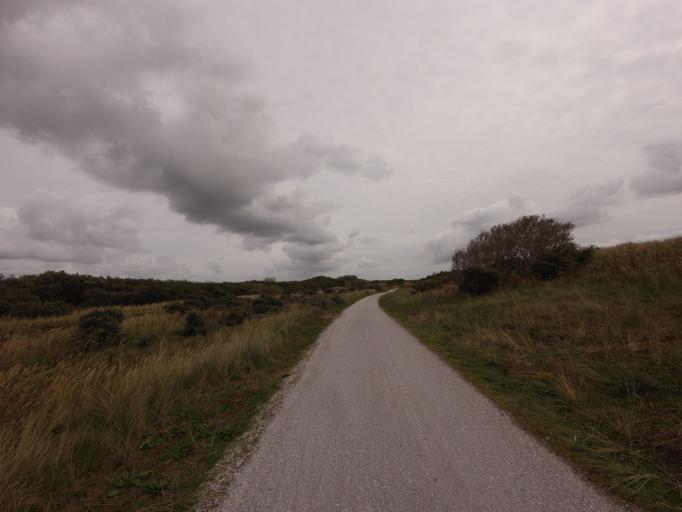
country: NL
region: Friesland
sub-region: Gemeente Ameland
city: Hollum
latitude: 53.4582
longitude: 5.6698
